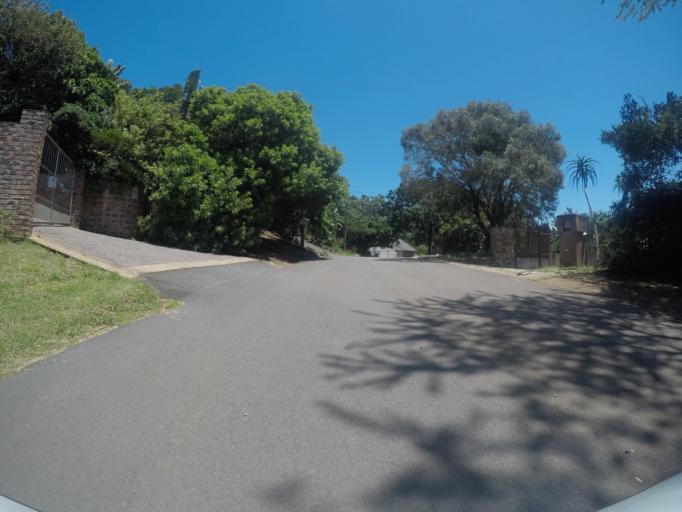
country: ZA
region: Eastern Cape
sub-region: Buffalo City Metropolitan Municipality
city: East London
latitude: -32.9329
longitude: 28.0081
